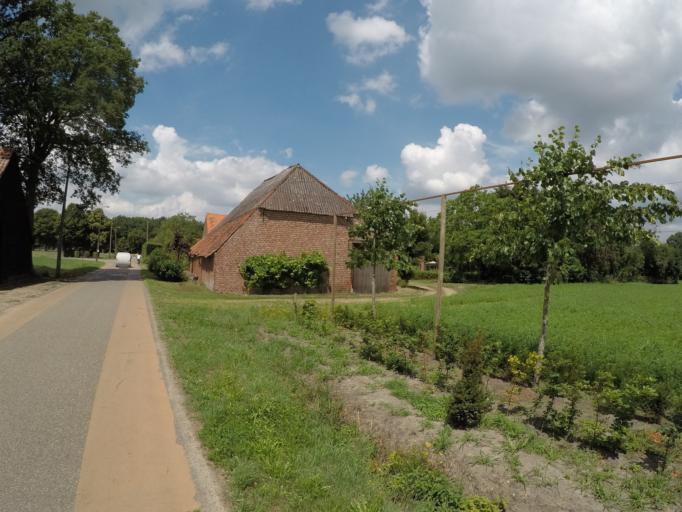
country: BE
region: Flanders
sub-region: Provincie Antwerpen
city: Beerse
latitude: 51.2784
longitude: 4.8488
